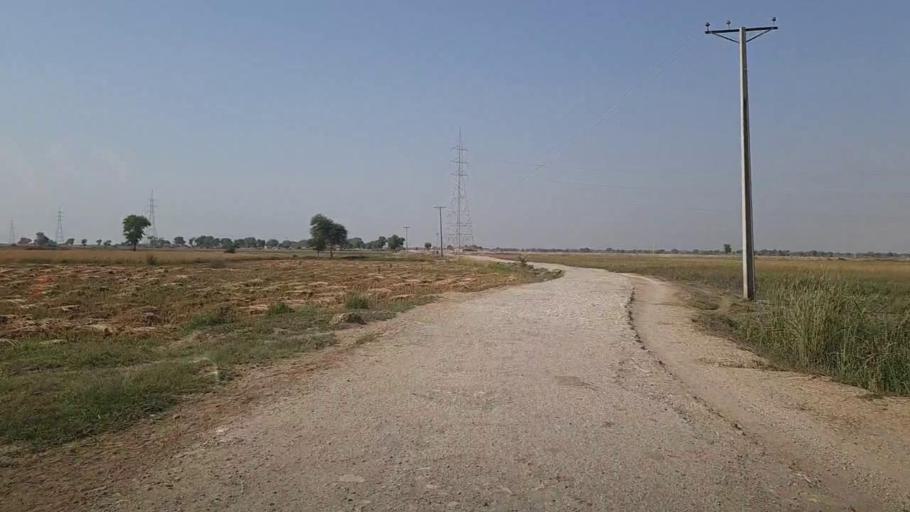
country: PK
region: Sindh
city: Kandhkot
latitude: 28.4101
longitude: 69.2457
